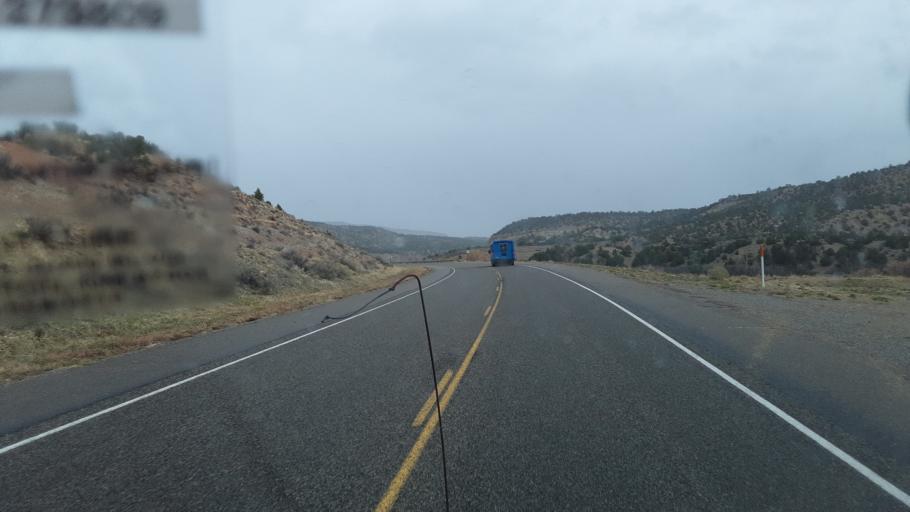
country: US
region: New Mexico
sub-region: Rio Arriba County
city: Santa Teresa
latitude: 36.3748
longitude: -106.5044
